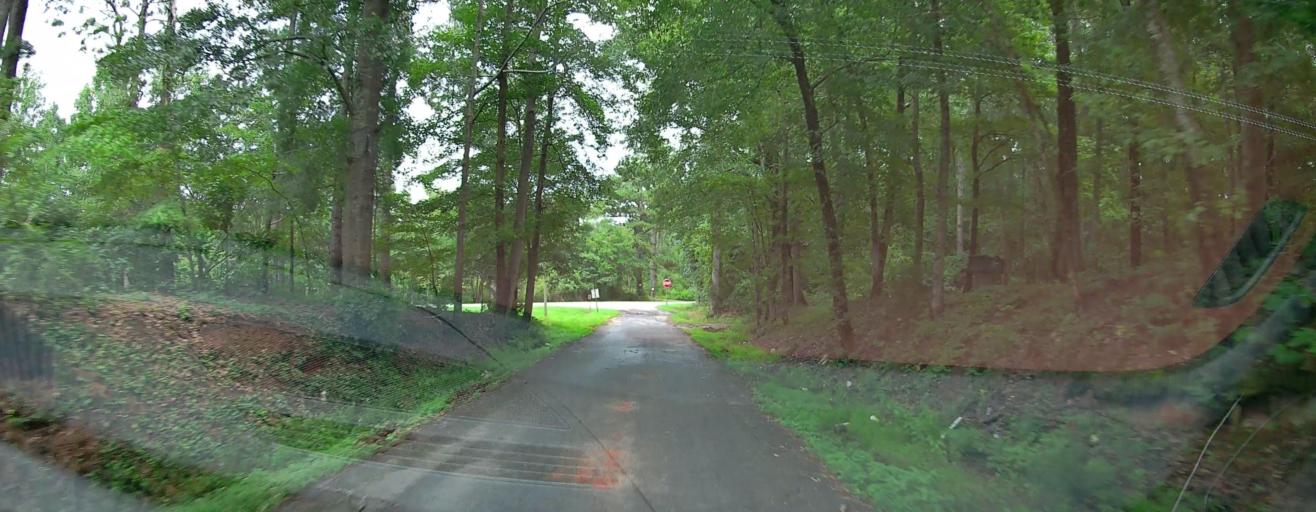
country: US
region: Georgia
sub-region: Twiggs County
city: Jeffersonville
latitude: 32.6789
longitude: -83.3224
